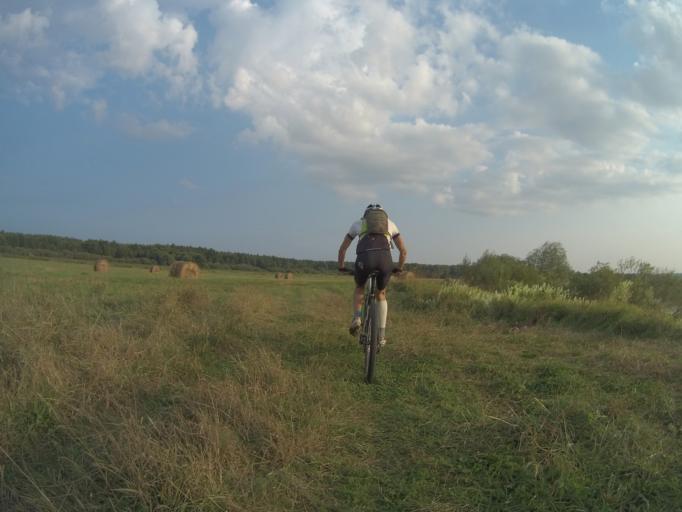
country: RU
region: Vladimir
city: Orgtrud
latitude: 56.3008
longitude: 40.6298
